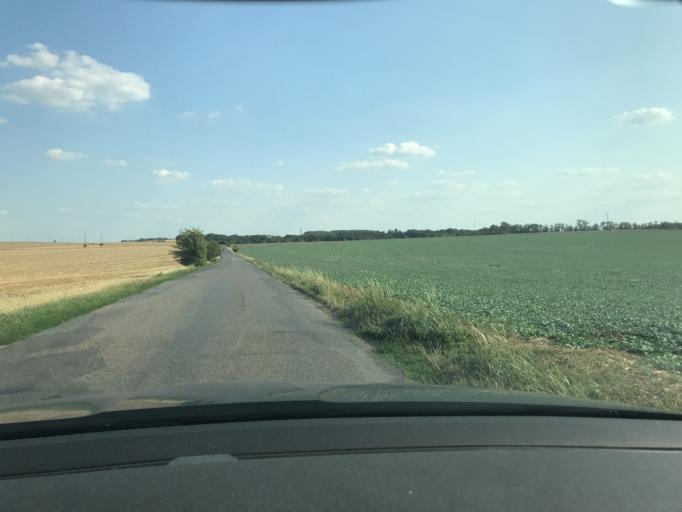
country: CZ
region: Central Bohemia
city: Kralupy nad Vltavou
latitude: 50.2261
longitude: 14.3215
